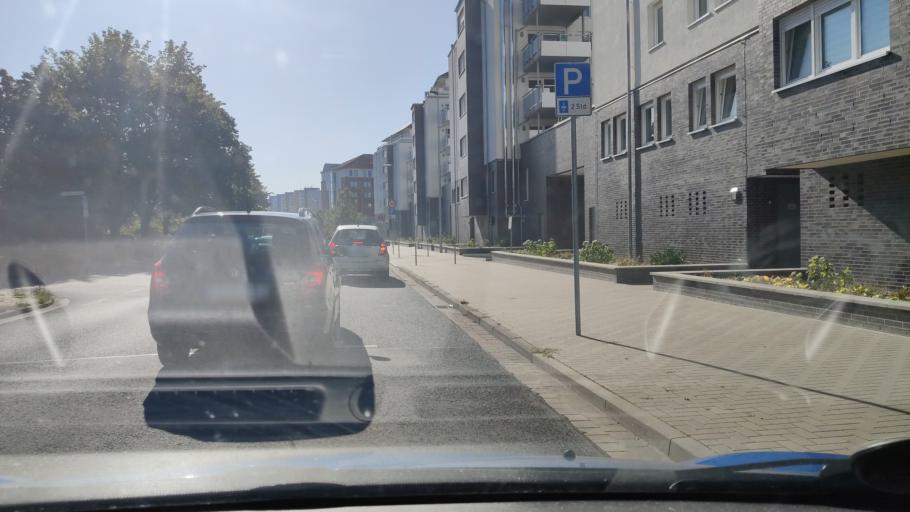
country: DE
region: Lower Saxony
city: Laatzen
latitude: 52.3118
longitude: 9.8080
